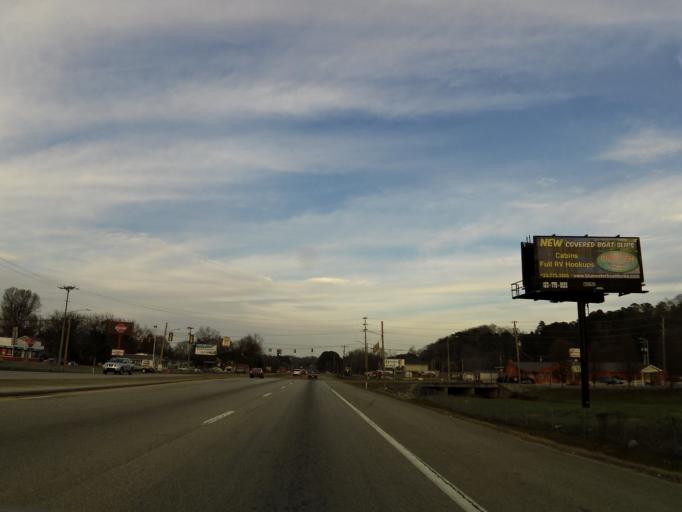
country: US
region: Tennessee
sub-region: Rhea County
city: Dayton
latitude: 35.4820
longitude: -85.0230
